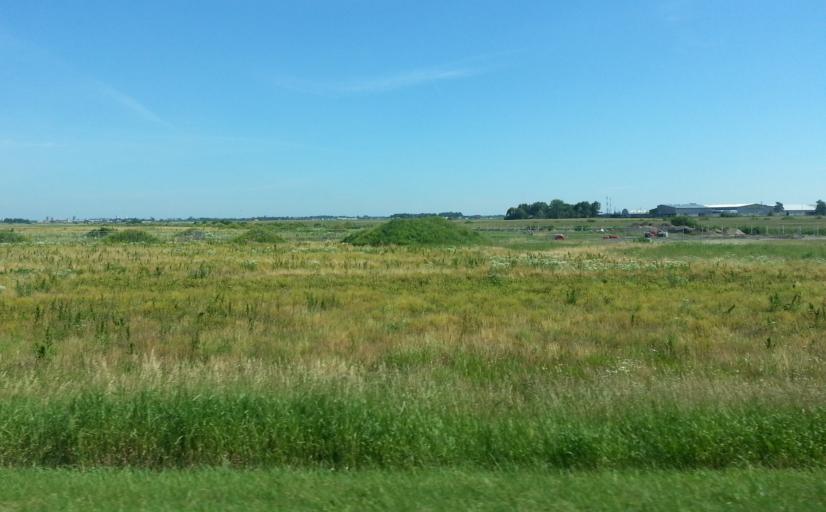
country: LT
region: Panevezys
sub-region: Panevezys City
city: Panevezys
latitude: 55.6714
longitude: 24.3434
